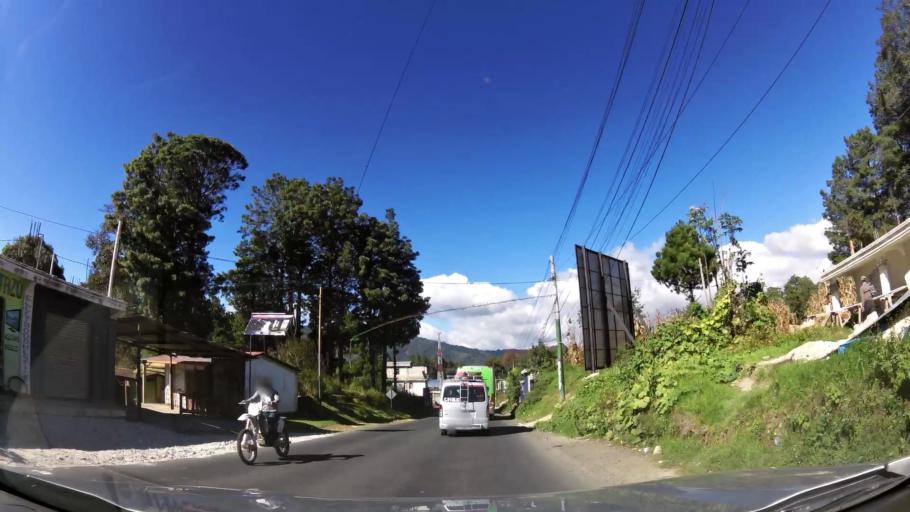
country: GT
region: Solola
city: Solola
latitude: 14.8026
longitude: -91.1796
